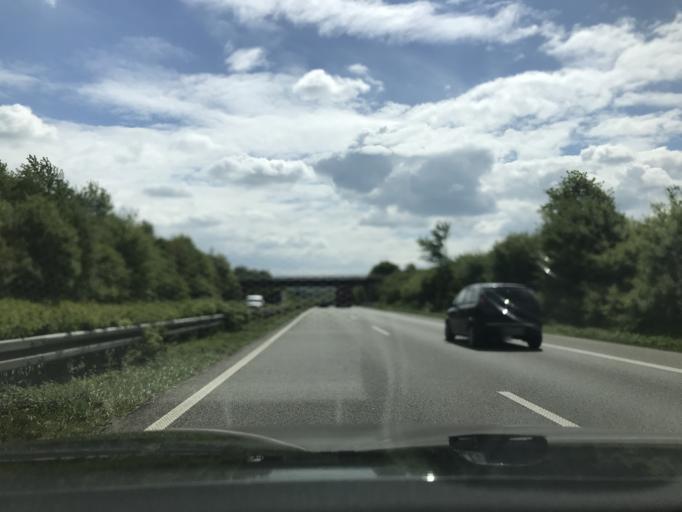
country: DE
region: Lower Saxony
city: Bissendorf
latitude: 52.1874
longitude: 8.1477
